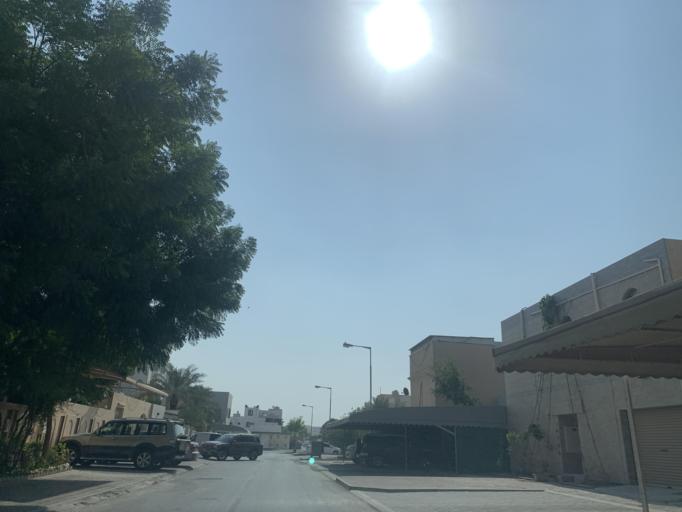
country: BH
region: Central Governorate
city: Madinat Hamad
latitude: 26.1262
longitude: 50.4908
